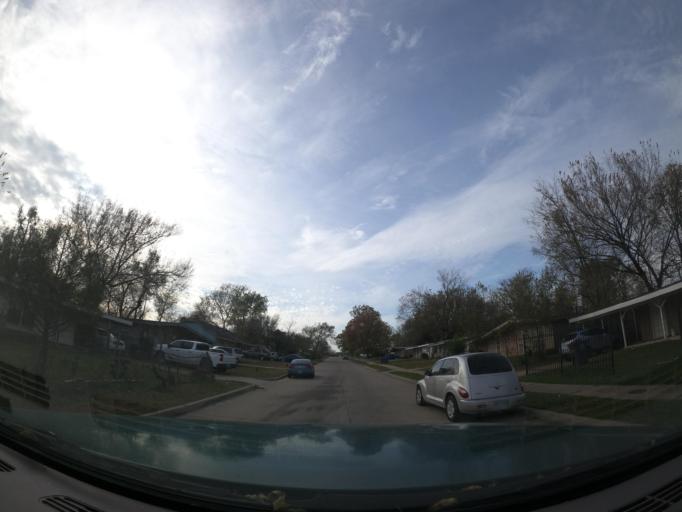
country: US
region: Oklahoma
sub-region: Tulsa County
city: Turley
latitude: 36.2314
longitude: -95.9907
